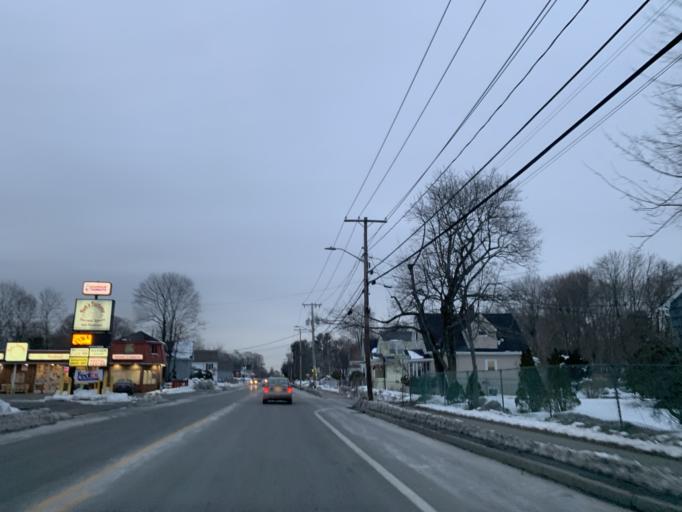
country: US
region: Massachusetts
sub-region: Norfolk County
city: Stoughton
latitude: 42.1204
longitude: -71.0914
